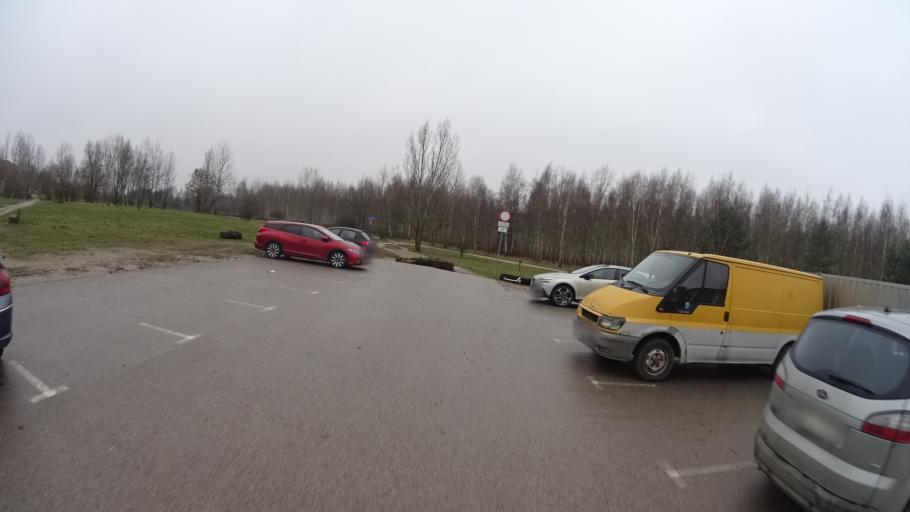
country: PL
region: Masovian Voivodeship
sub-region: Warszawa
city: Ursynow
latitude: 52.1378
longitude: 21.0389
